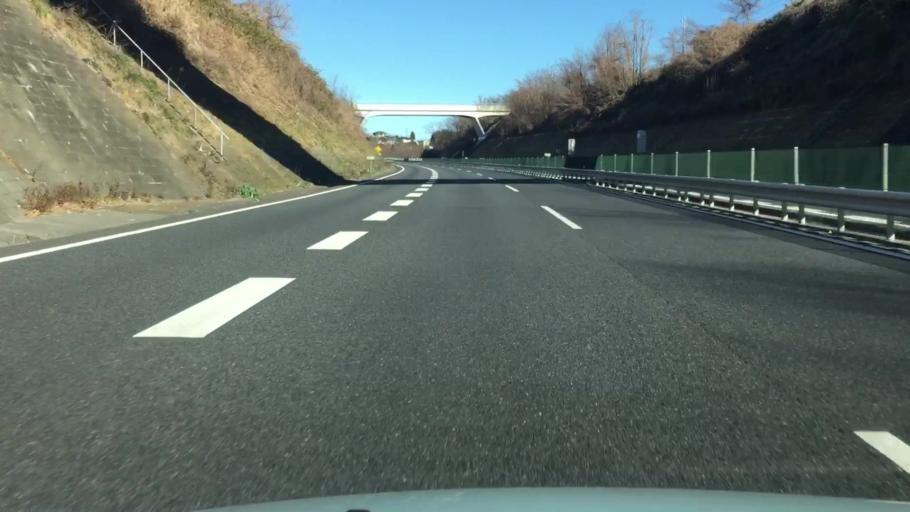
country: JP
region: Gunma
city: Shibukawa
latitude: 36.4874
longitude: 139.0296
